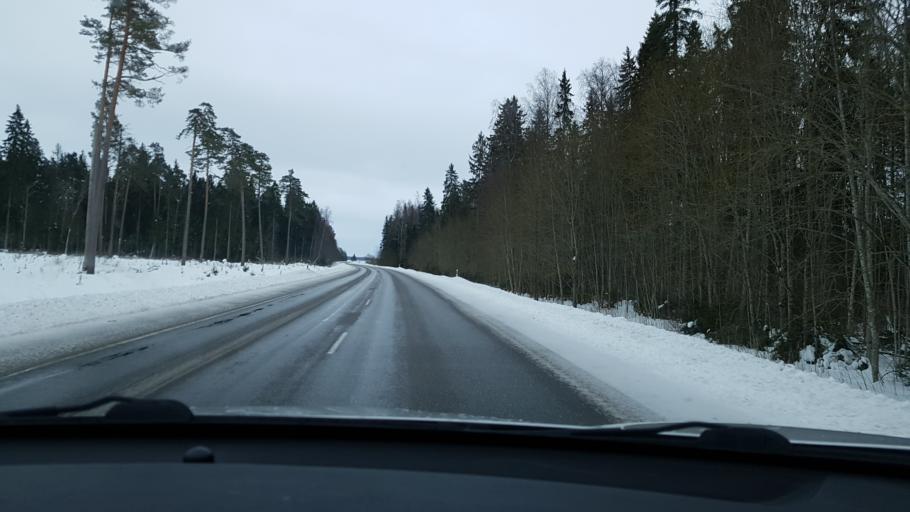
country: EE
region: Jaervamaa
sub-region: Jaerva-Jaani vald
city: Jarva-Jaani
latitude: 59.0966
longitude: 25.8210
